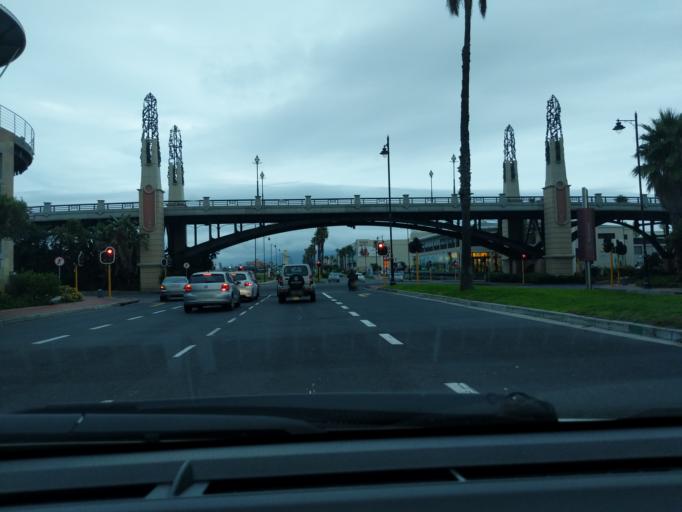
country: ZA
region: Western Cape
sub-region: City of Cape Town
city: Sunset Beach
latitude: -33.8915
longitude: 18.5165
